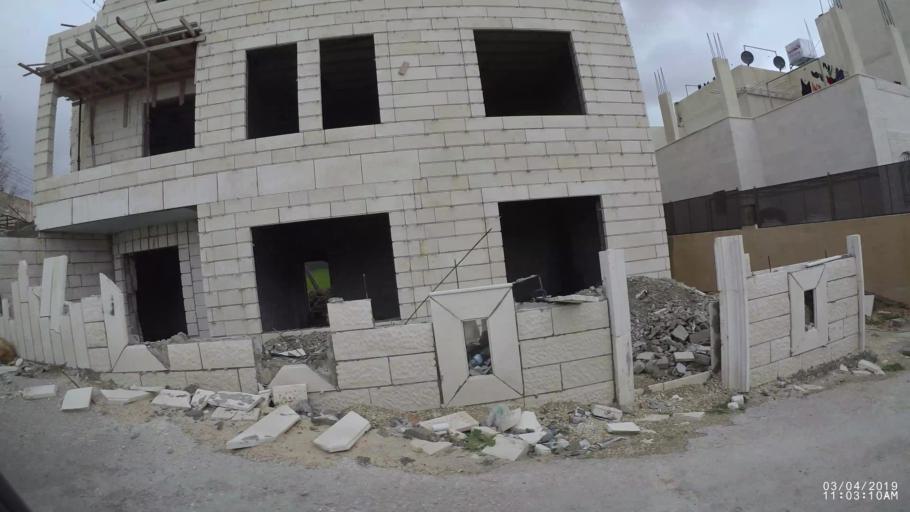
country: JO
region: Amman
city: Wadi as Sir
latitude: 31.9455
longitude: 35.8150
